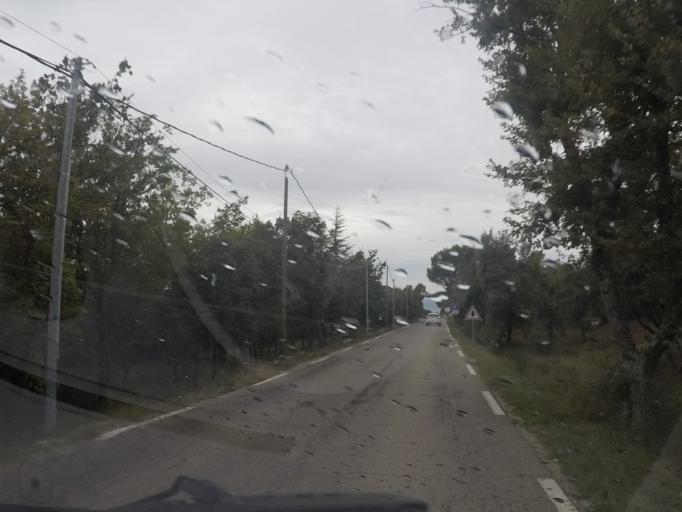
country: FR
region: Provence-Alpes-Cote d'Azur
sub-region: Departement du Vaucluse
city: Bonnieux
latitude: 43.8178
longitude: 5.3193
